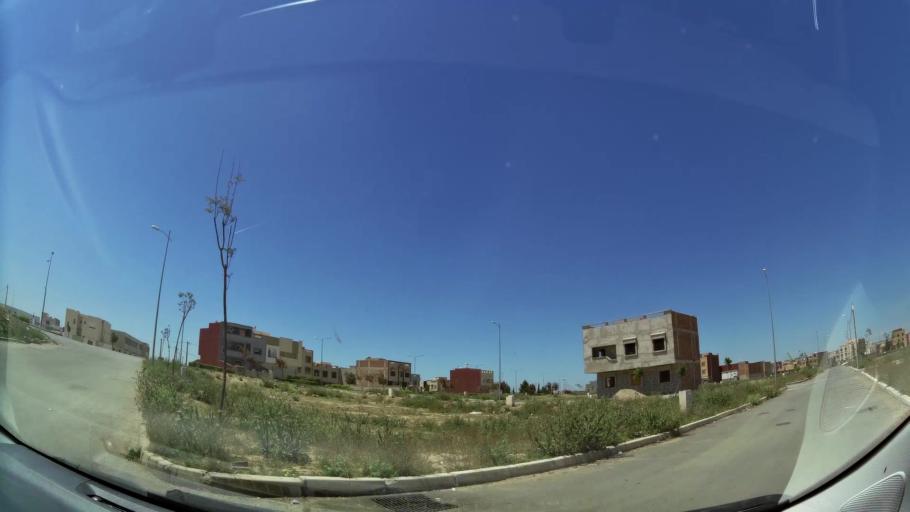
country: MA
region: Oriental
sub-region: Oujda-Angad
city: Oujda
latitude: 34.6739
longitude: -1.8655
